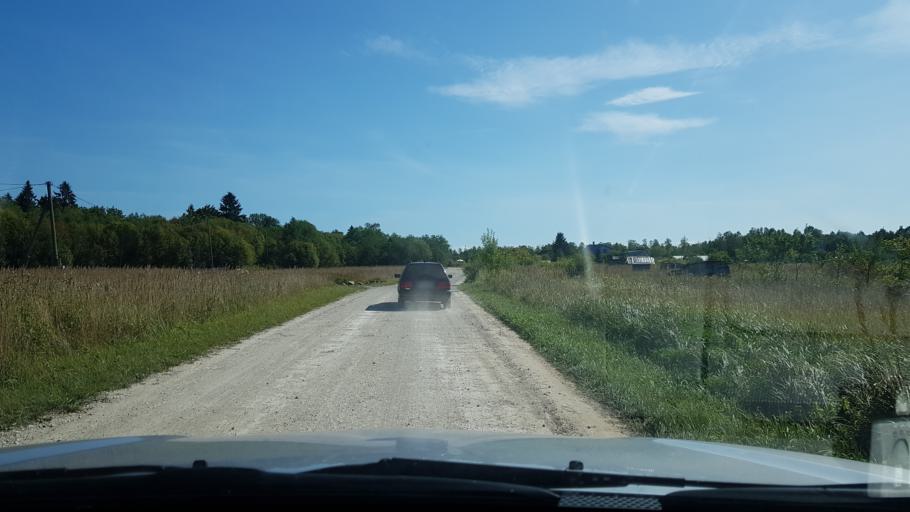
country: EE
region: Ida-Virumaa
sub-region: Sillamaee linn
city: Sillamae
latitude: 59.3738
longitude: 27.7850
